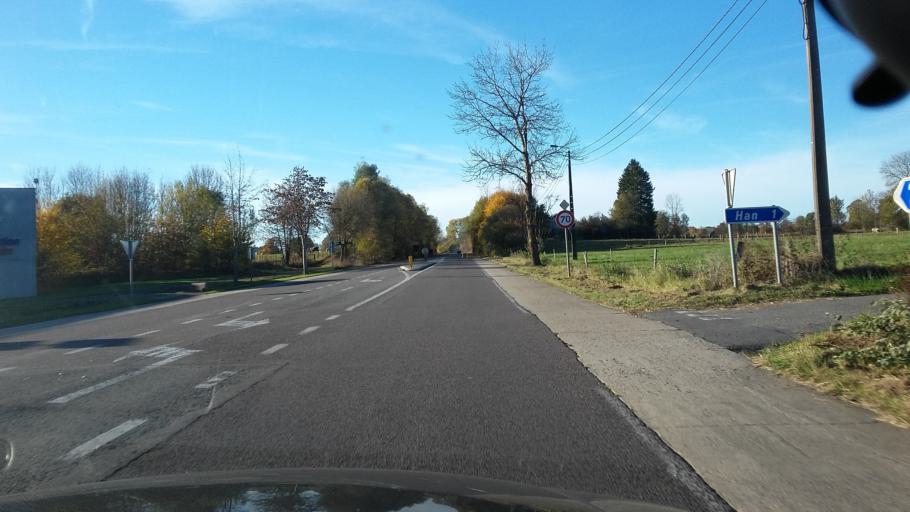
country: BE
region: Wallonia
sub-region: Province du Luxembourg
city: Tintigny
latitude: 49.6774
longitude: 5.5406
